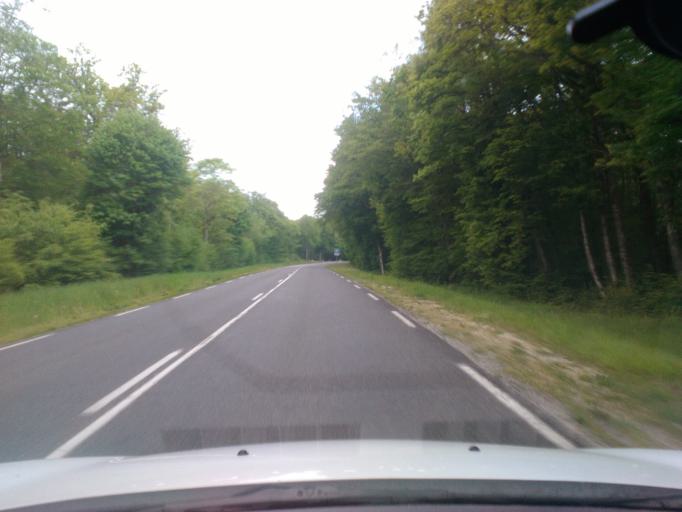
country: FR
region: Champagne-Ardenne
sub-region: Departement de la Haute-Marne
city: Lavilleneuve-au-Roi
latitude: 48.2133
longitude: 4.9155
